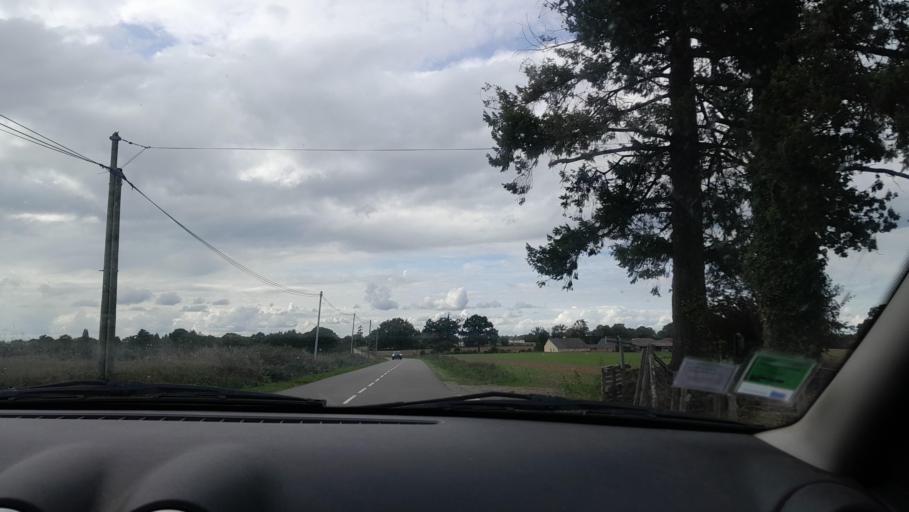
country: FR
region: Brittany
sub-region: Departement d'Ille-et-Vilaine
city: Argentre-du-Plessis
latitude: 48.0533
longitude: -1.1196
